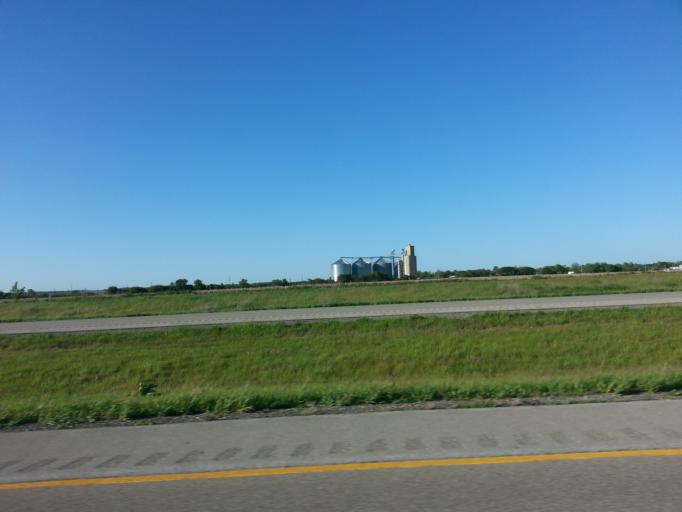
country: US
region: Illinois
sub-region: McLean County
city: Le Roy
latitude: 40.3447
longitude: -88.7783
